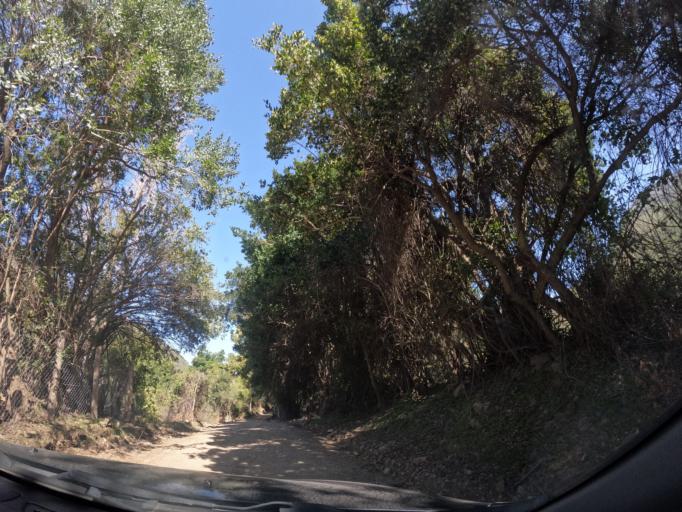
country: CL
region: Maule
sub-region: Provincia de Linares
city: Longavi
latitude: -36.2814
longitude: -71.4167
